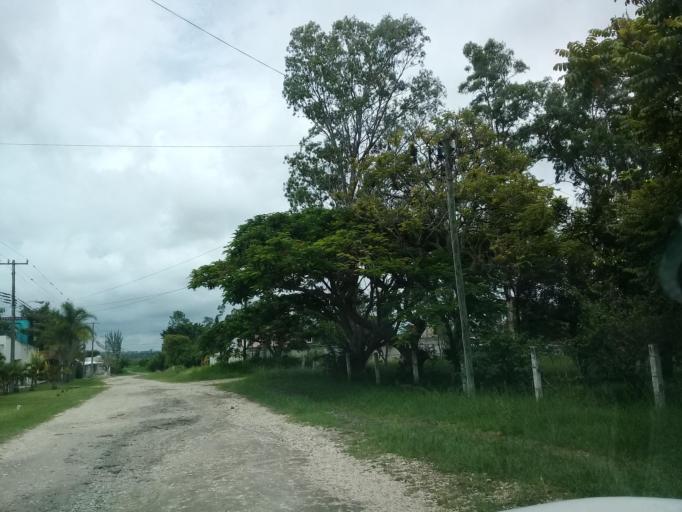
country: MX
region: Veracruz
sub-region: Emiliano Zapata
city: Dos Rios
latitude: 19.4832
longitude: -96.7940
